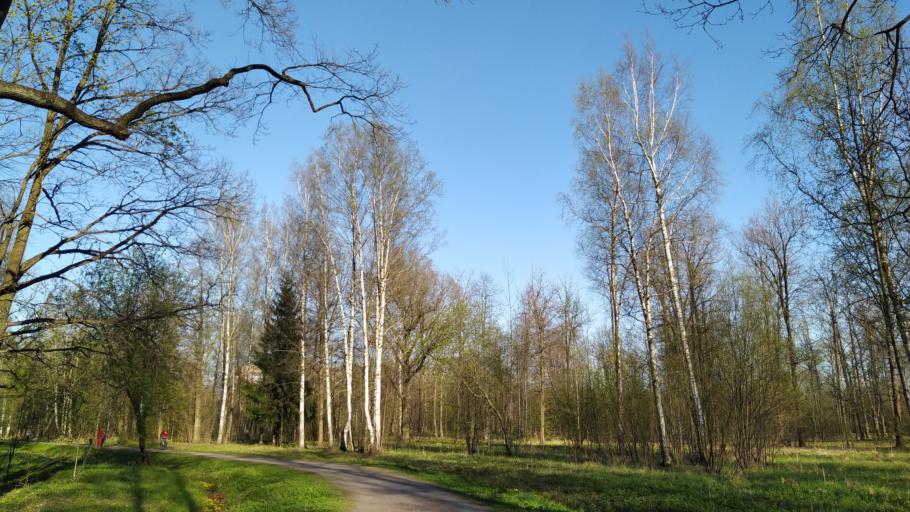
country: RU
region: St.-Petersburg
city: Aleksandrovskaya
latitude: 59.7053
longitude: 30.3507
